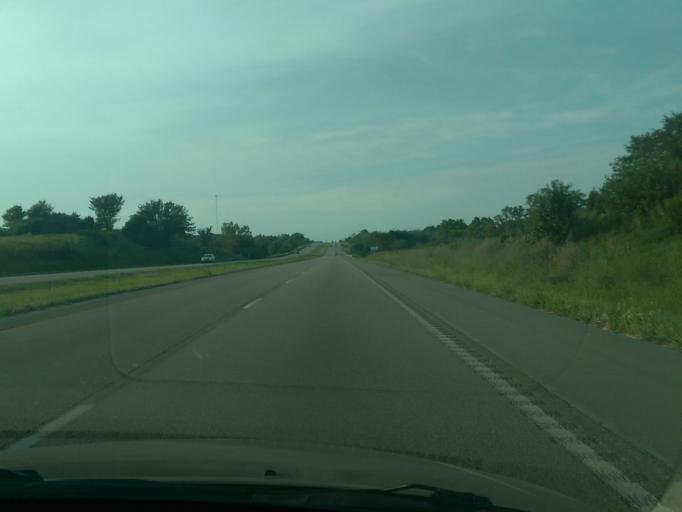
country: US
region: Missouri
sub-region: Platte County
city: Platte City
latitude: 39.4040
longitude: -94.7895
